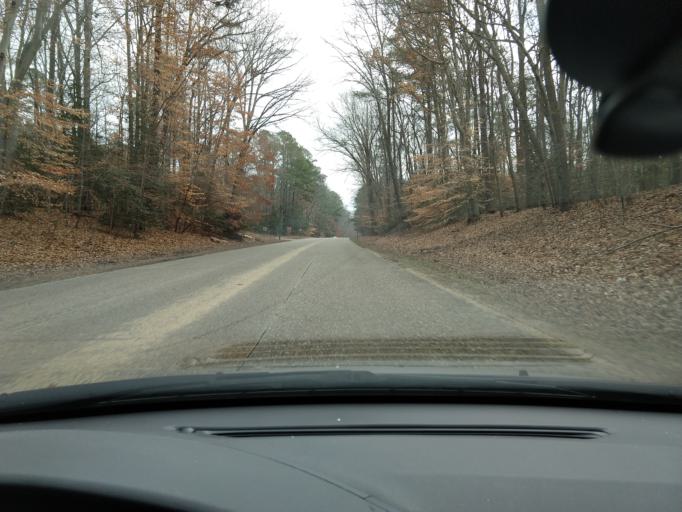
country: US
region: Virginia
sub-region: City of Williamsburg
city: Williamsburg
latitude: 37.2788
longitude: -76.6750
